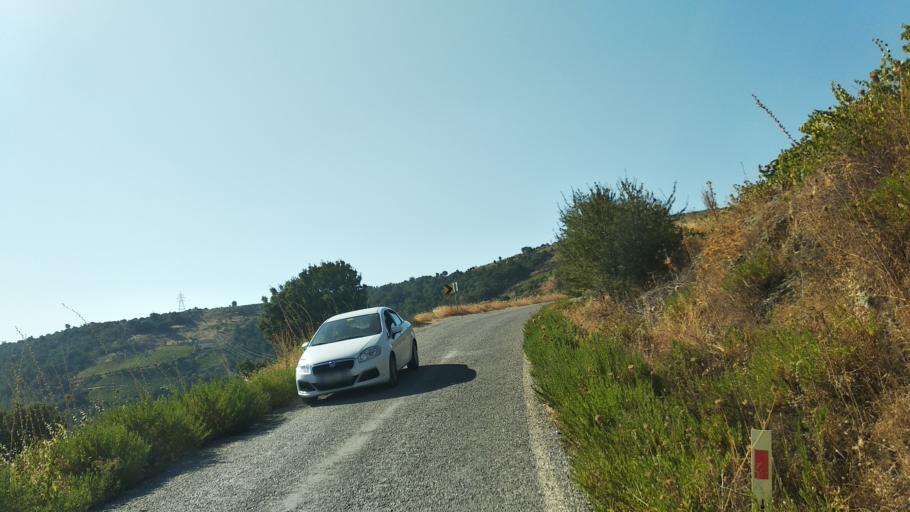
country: TR
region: Izmir
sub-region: Seferihisar
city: Seferhisar
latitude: 38.3258
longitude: 26.9515
